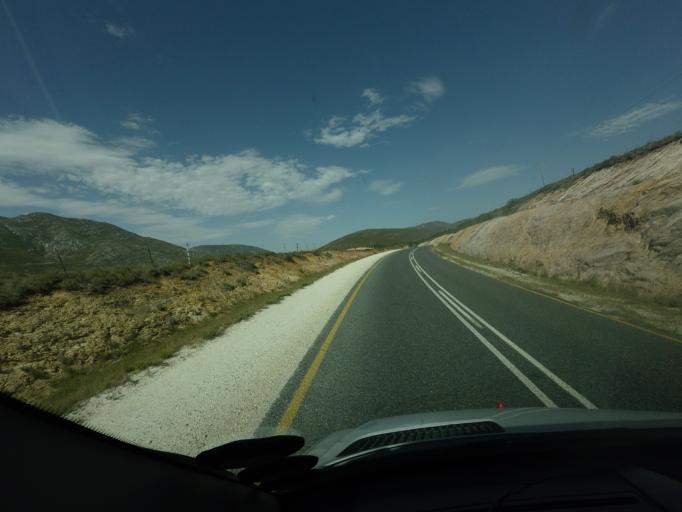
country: ZA
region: Western Cape
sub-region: Overberg District Municipality
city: Caledon
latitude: -34.4125
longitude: 19.5562
